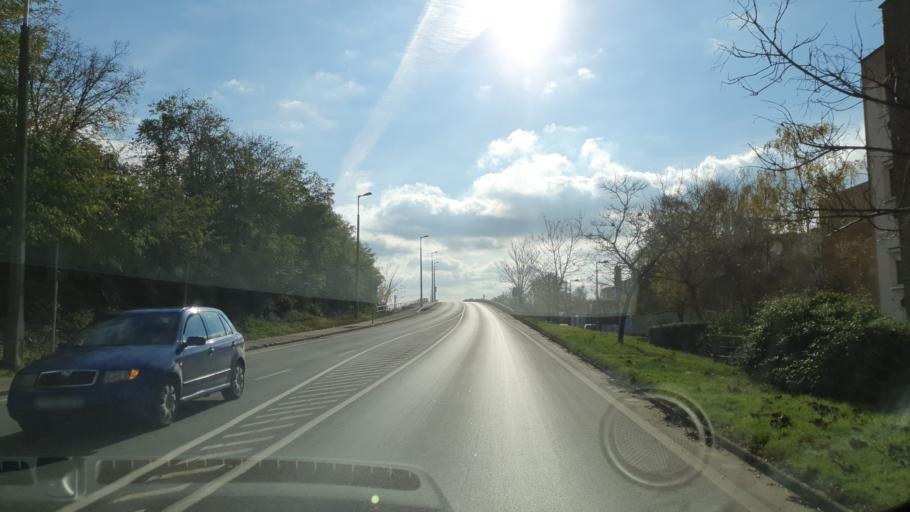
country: HU
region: Szabolcs-Szatmar-Bereg
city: Kisvarda
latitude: 48.2154
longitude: 22.0836
